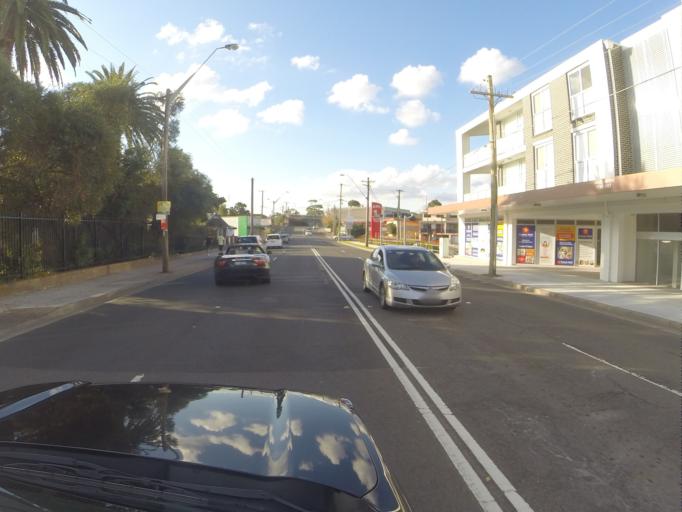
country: AU
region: New South Wales
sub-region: Rockdale
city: Bexley
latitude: -33.9646
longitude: 151.1114
